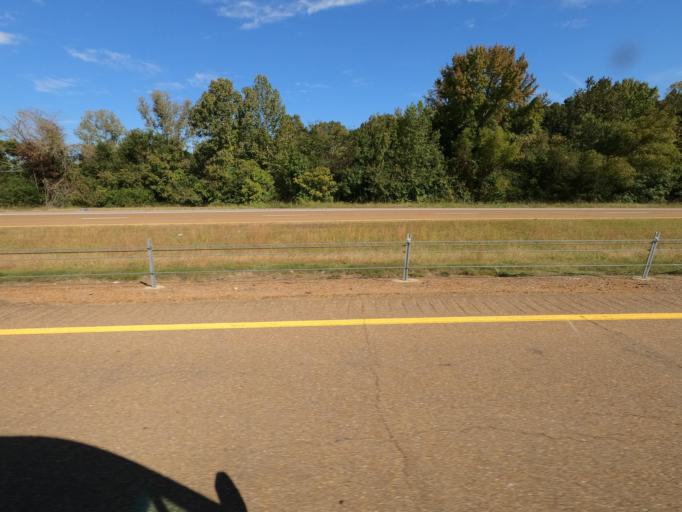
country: US
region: Tennessee
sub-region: Shelby County
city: Lakeland
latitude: 35.3106
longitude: -89.7709
